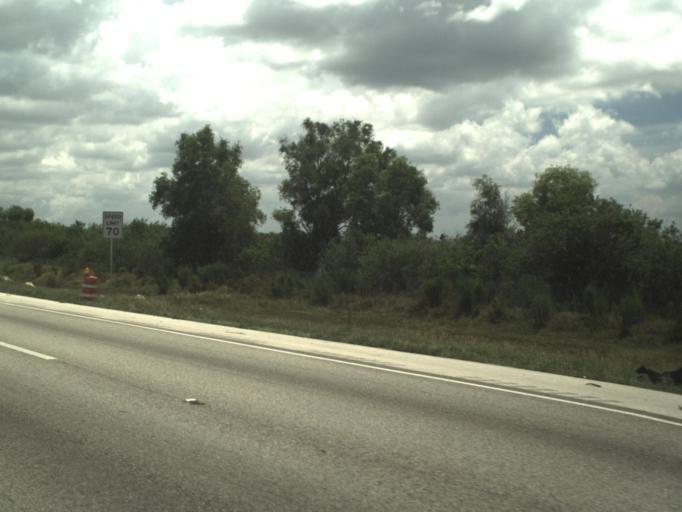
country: US
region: Florida
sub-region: Broward County
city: Weston
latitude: 26.1066
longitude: -80.3563
